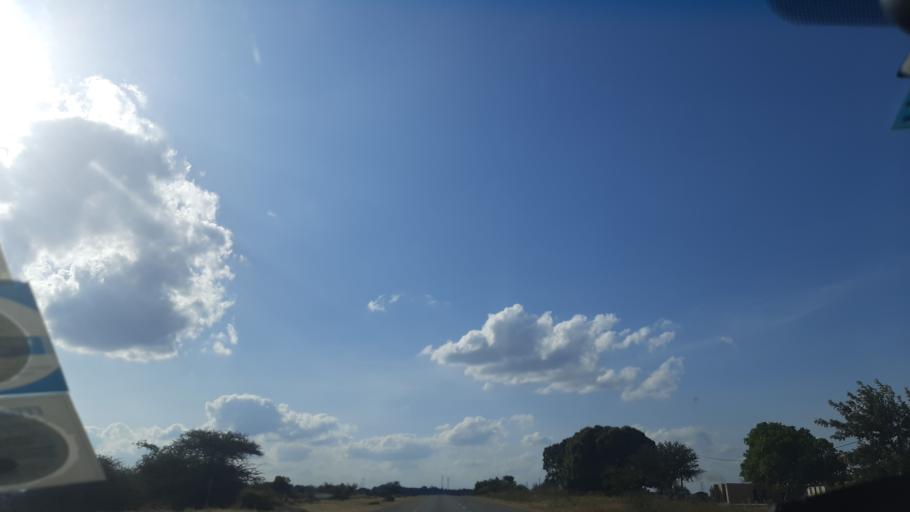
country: TZ
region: Singida
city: Ikungi
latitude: -5.1577
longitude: 34.7777
